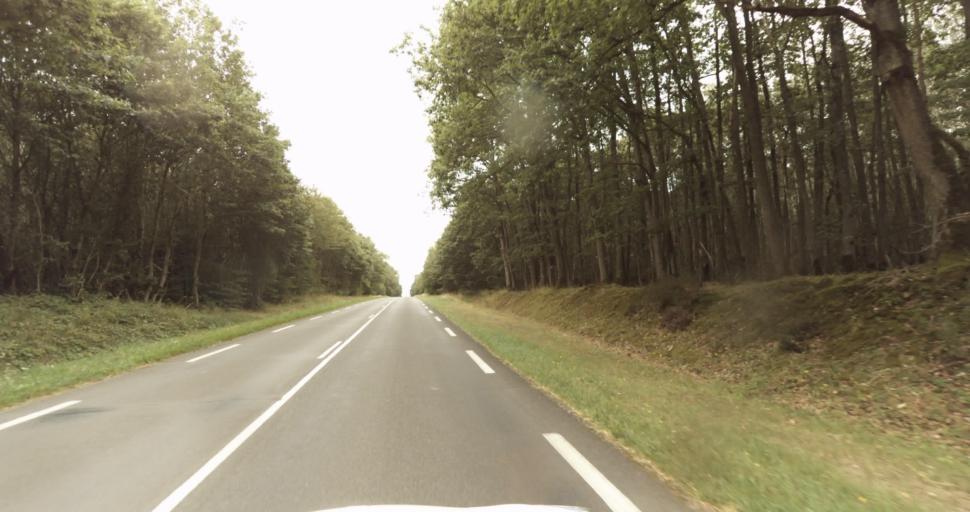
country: FR
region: Haute-Normandie
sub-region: Departement de l'Eure
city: La Madeleine-de-Nonancourt
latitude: 48.8162
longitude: 1.1871
